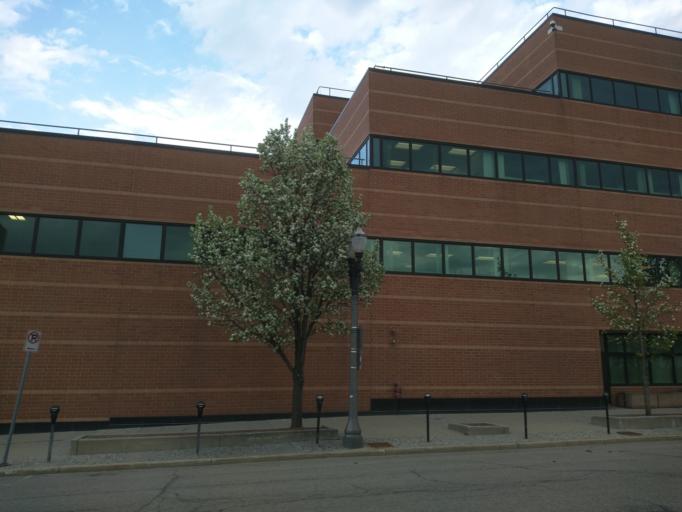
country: US
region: Michigan
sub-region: Ingham County
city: Lansing
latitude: 42.7279
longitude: -84.5523
